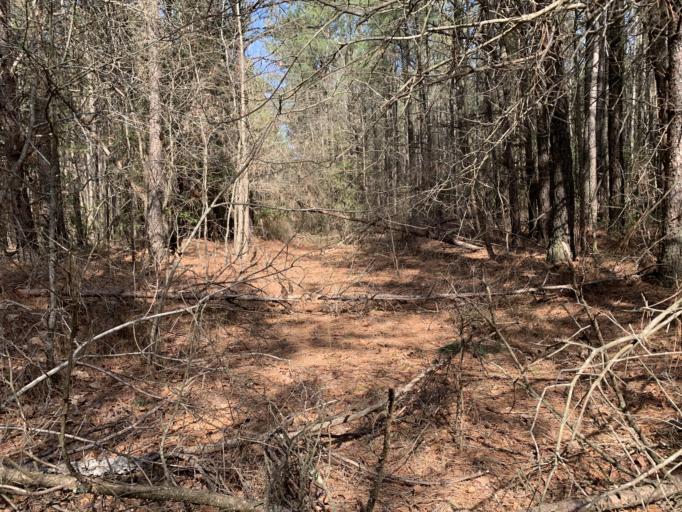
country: US
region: Delaware
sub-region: Sussex County
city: Georgetown
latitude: 38.6819
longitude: -75.4746
